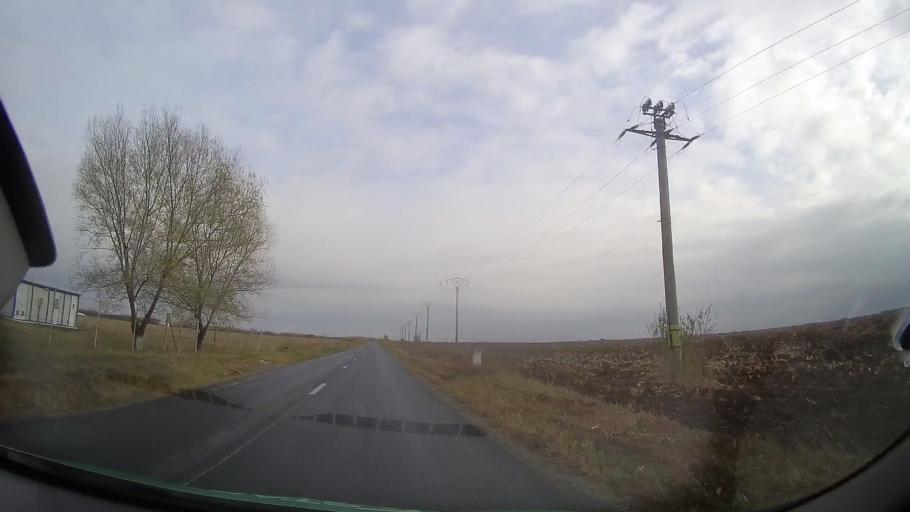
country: RO
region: Ialomita
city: Brazii
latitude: 44.7569
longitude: 26.3722
